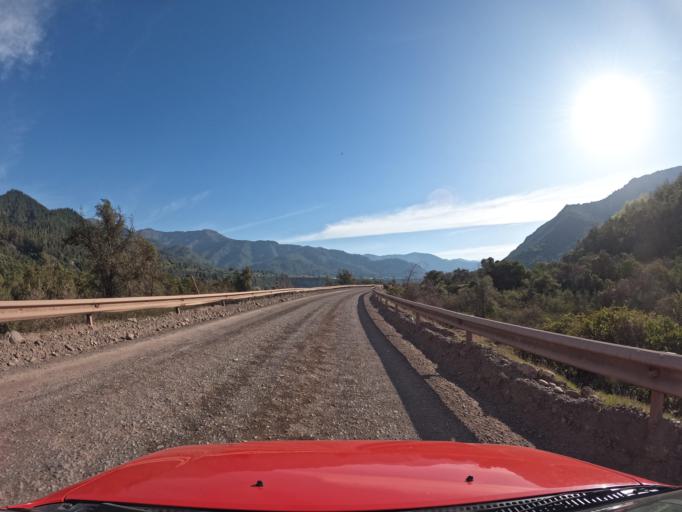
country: CL
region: Maule
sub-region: Provincia de Curico
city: Teno
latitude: -35.0013
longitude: -70.8278
